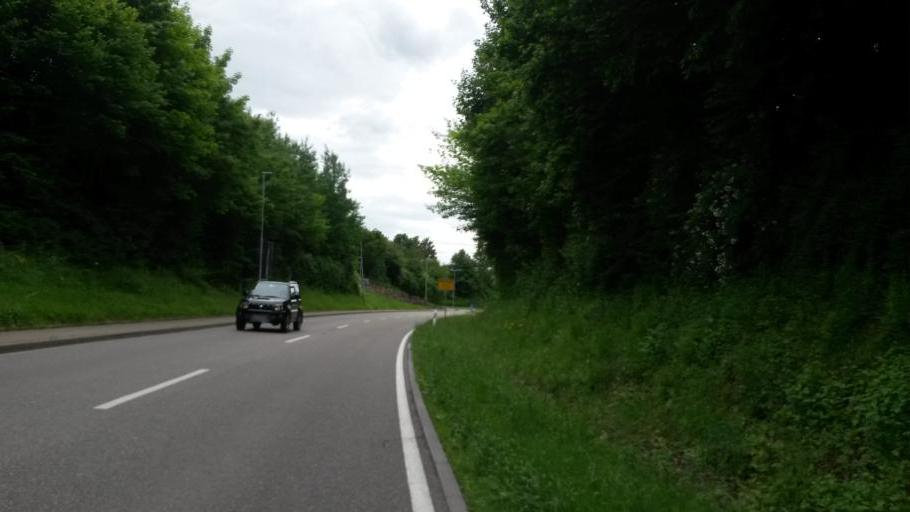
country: DE
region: Baden-Wuerttemberg
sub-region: Karlsruhe Region
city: Konigsbach-Stein
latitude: 48.9513
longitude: 8.5806
